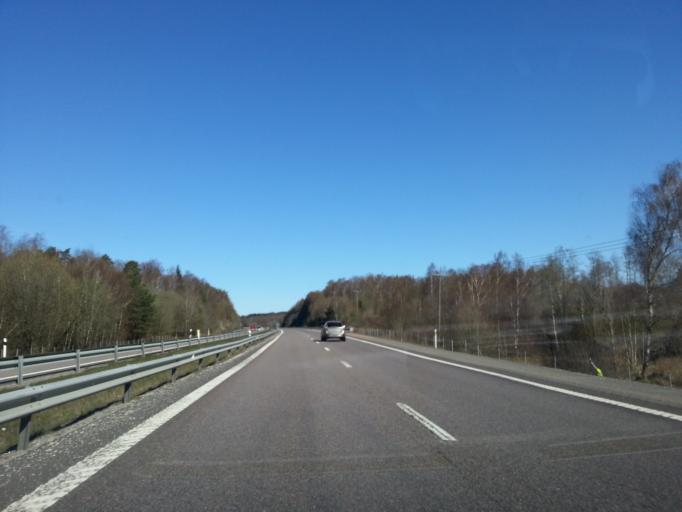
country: SE
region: Vaestra Goetaland
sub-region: Kungalvs Kommun
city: Kode
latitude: 57.9277
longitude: 11.8759
